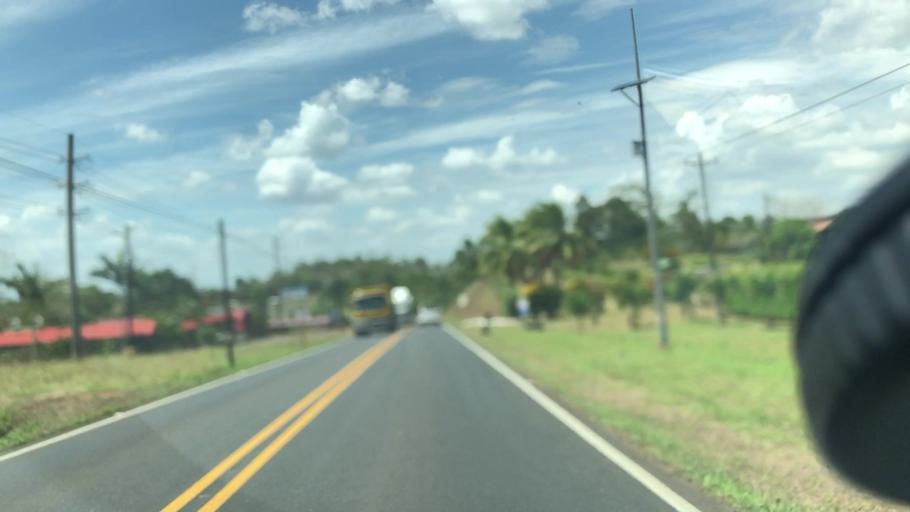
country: CR
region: Alajuela
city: Pital
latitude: 10.4571
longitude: -84.3873
